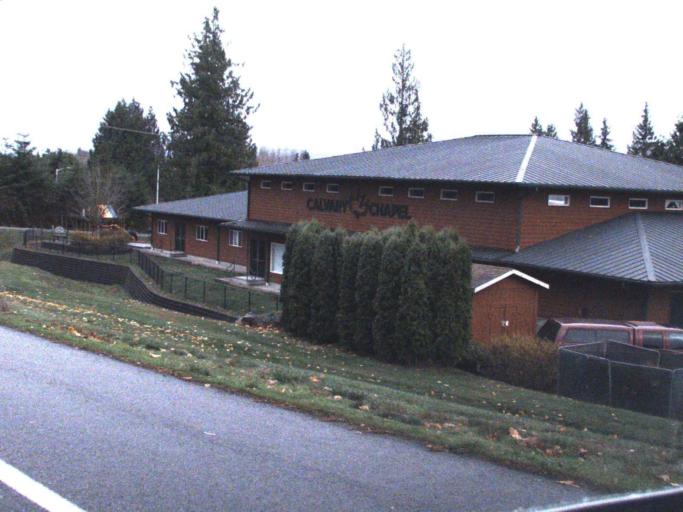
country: US
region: Washington
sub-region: Snohomish County
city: West Lake Stevens
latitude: 47.9917
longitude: -122.1045
